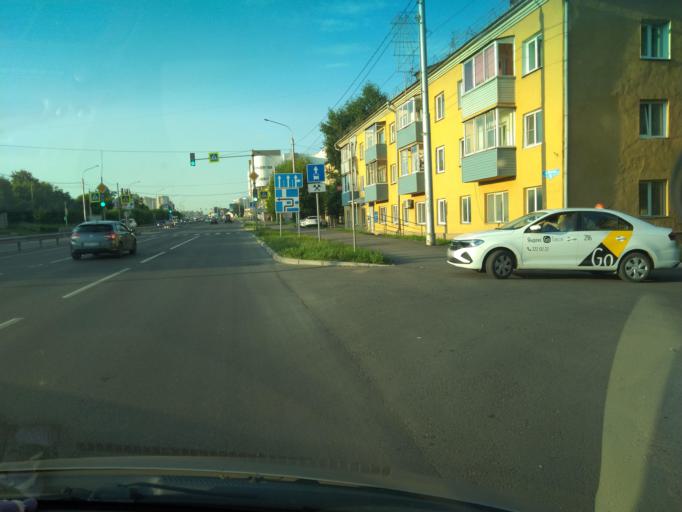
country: RU
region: Krasnoyarskiy
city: Krasnoyarsk
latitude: 56.0268
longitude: 92.8877
